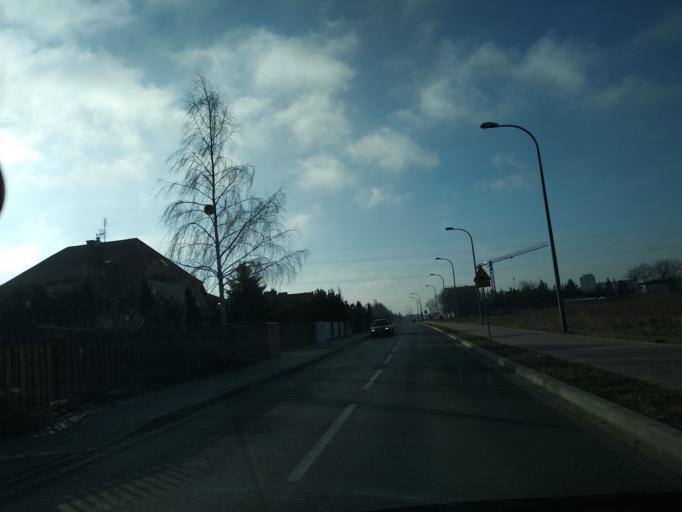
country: PL
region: Masovian Voivodeship
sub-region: Powiat piaseczynski
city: Mysiadlo
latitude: 52.0903
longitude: 21.0128
